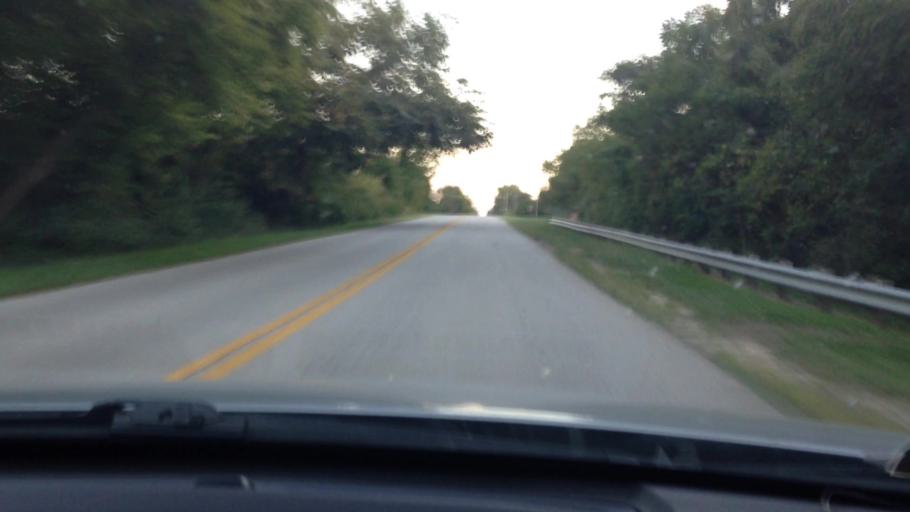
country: US
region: Kansas
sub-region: Leavenworth County
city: Lansing
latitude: 39.1825
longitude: -94.8267
